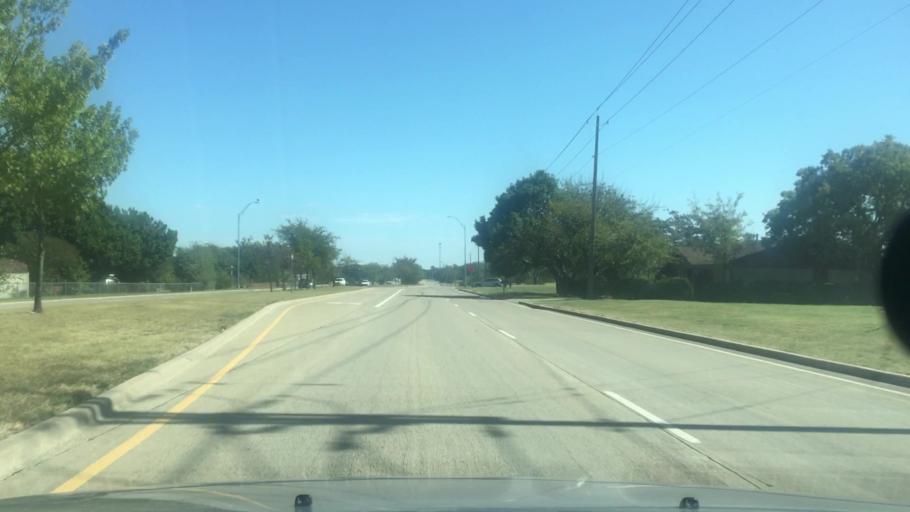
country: US
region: Texas
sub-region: Denton County
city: Denton
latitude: 33.2465
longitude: -97.1446
